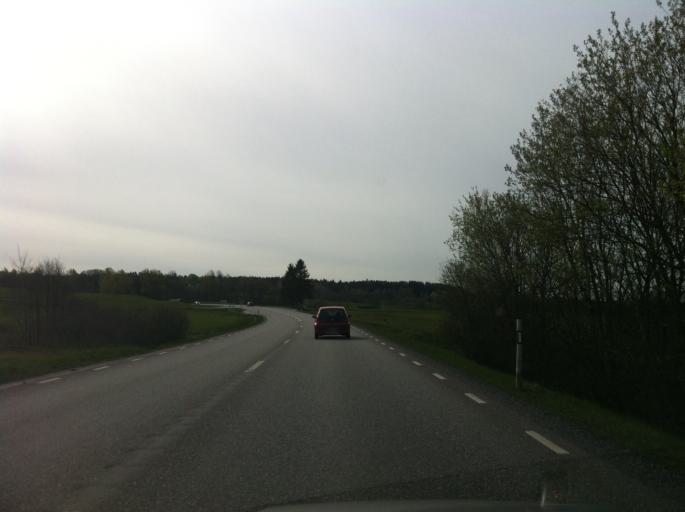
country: SE
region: Vaestra Goetaland
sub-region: Harryda Kommun
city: Ravlanda
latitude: 57.5259
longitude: 12.5403
